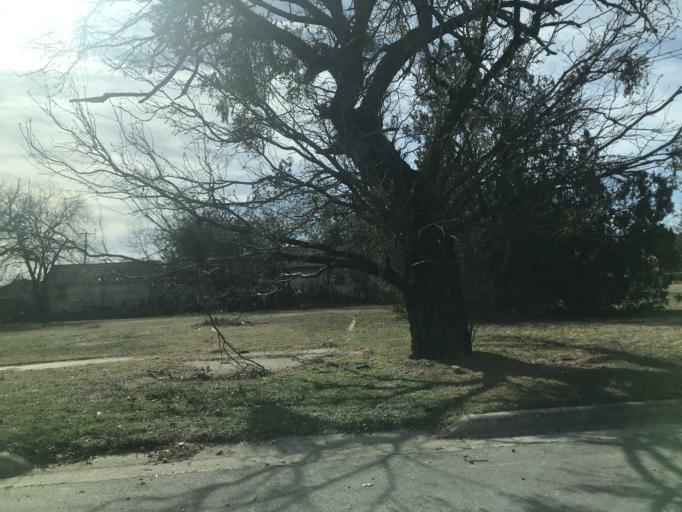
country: US
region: Texas
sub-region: Taylor County
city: Abilene
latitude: 32.4446
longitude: -99.7362
